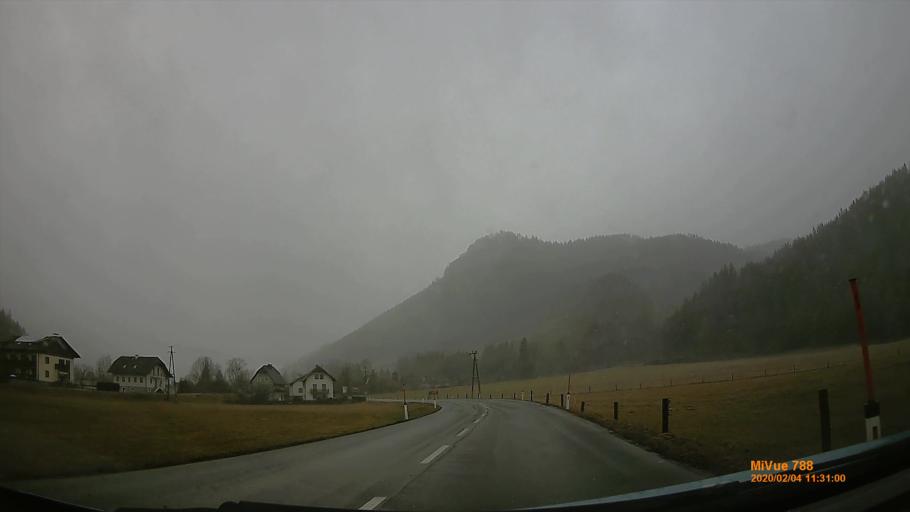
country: AT
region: Styria
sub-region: Politischer Bezirk Bruck-Muerzzuschlag
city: Neuberg an der Muerz
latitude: 47.6570
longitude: 15.5949
